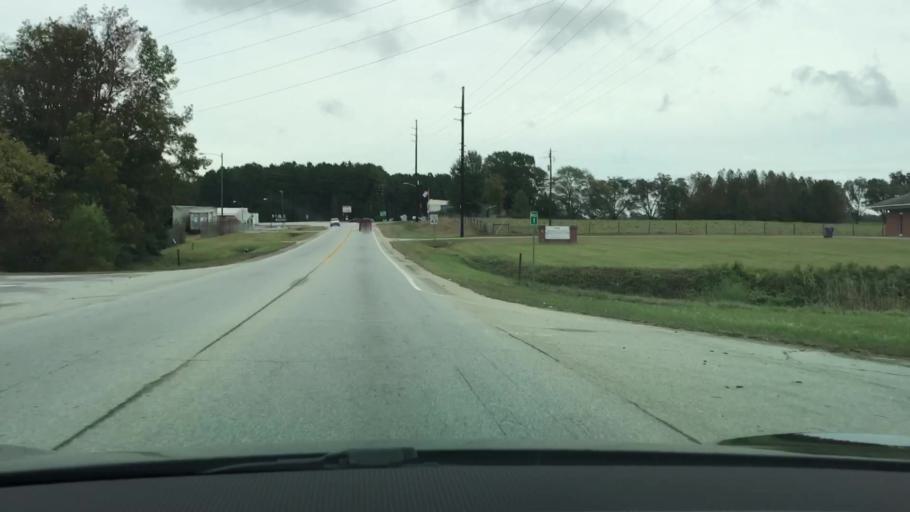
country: US
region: Georgia
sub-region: Warren County
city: Warrenton
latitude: 33.4004
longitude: -82.6590
